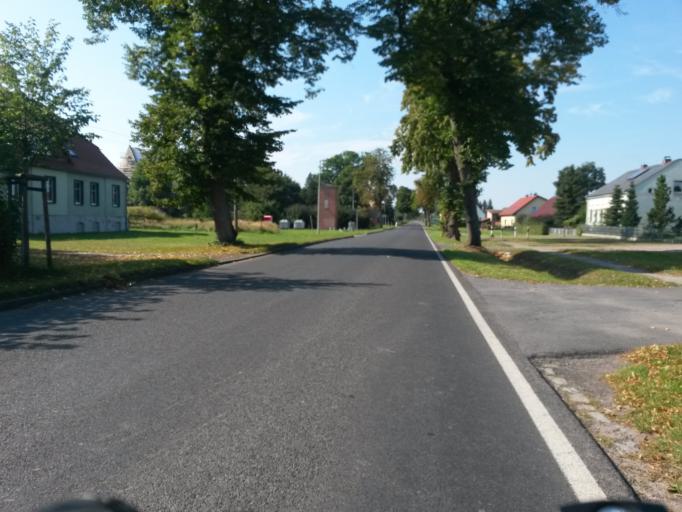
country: DE
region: Brandenburg
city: Templin
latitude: 53.0721
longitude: 13.4333
